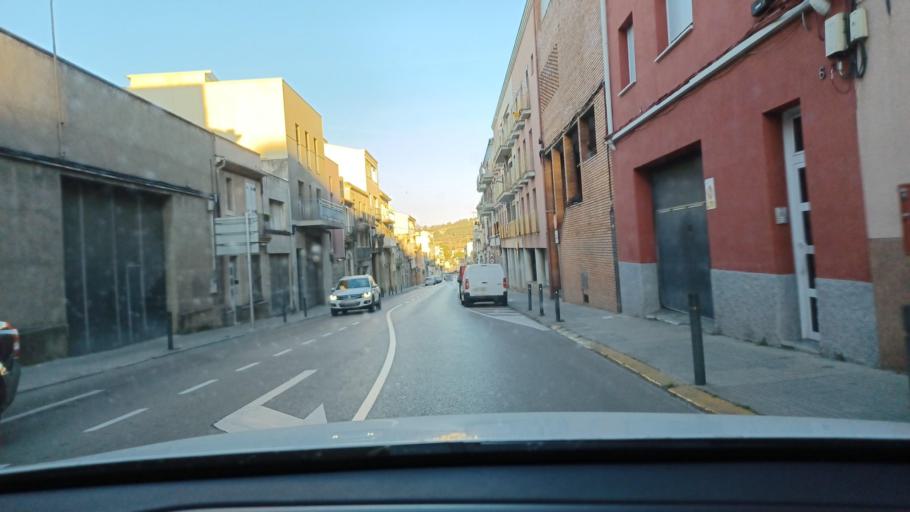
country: ES
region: Catalonia
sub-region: Provincia de Barcelona
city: Vilafranca del Penedes
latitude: 41.3470
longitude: 1.6944
